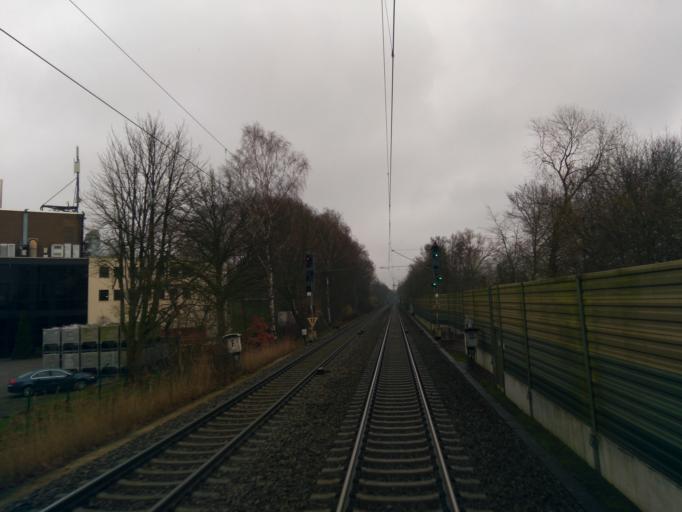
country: DE
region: Lower Saxony
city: Lilienthal
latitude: 53.0919
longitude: 8.9150
